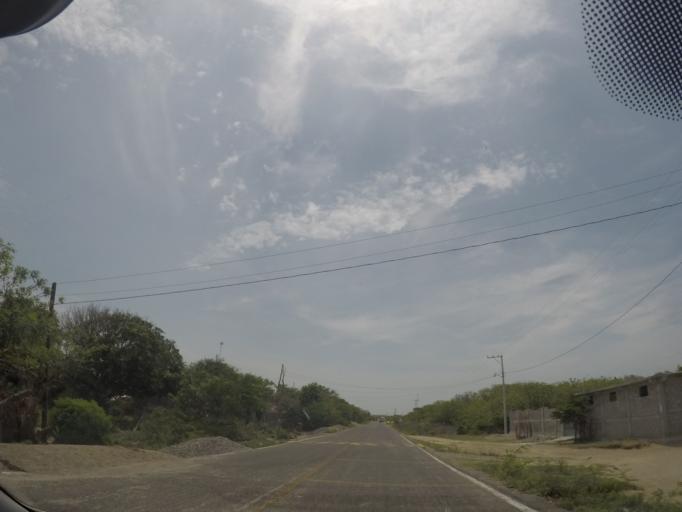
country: MX
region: Oaxaca
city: San Mateo del Mar
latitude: 16.2088
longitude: -94.9971
